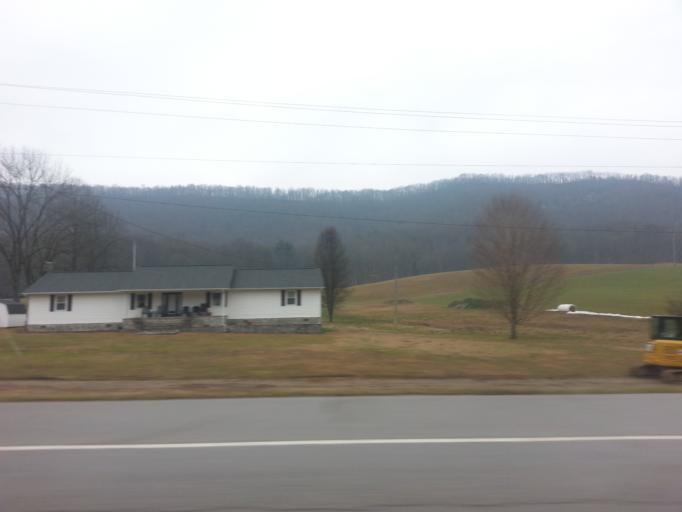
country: US
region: Tennessee
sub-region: Roane County
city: Harriman
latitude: 35.9756
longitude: -84.4889
